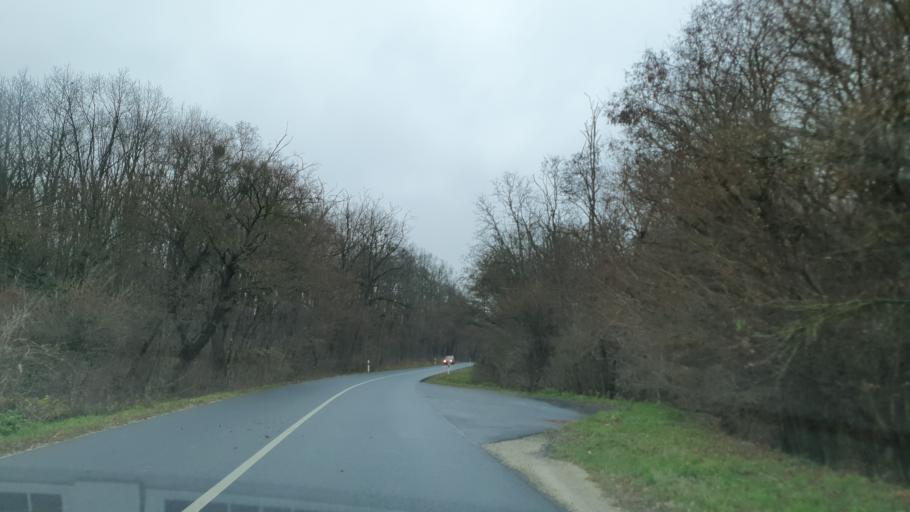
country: HU
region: Veszprem
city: Sumeg
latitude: 46.9205
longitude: 17.2455
